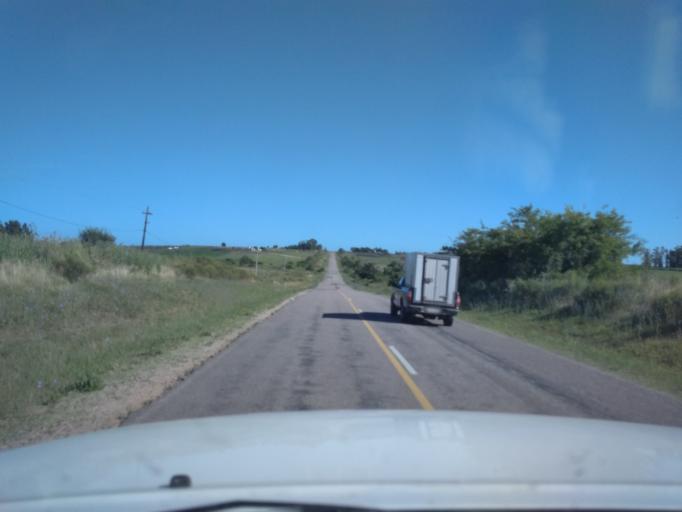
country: UY
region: Canelones
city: San Ramon
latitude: -34.1752
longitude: -55.9433
